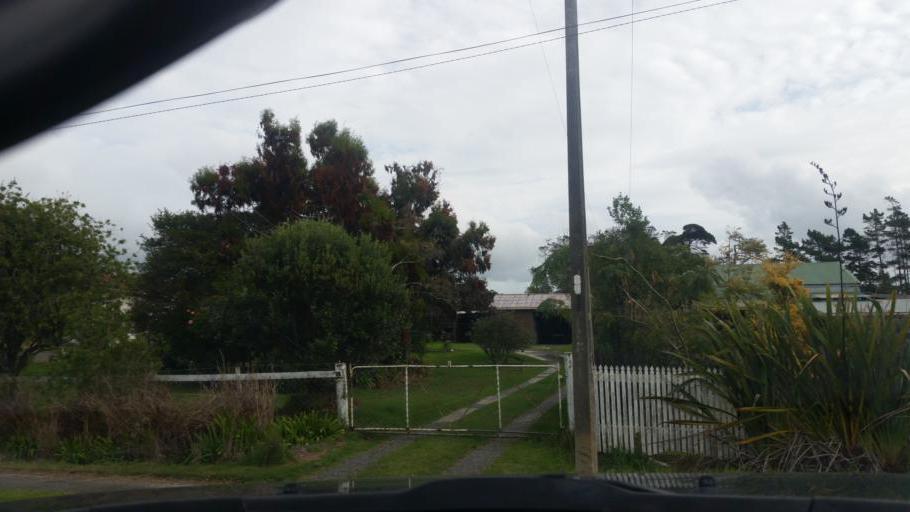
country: NZ
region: Northland
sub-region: Kaipara District
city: Dargaville
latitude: -36.0298
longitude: 173.9166
